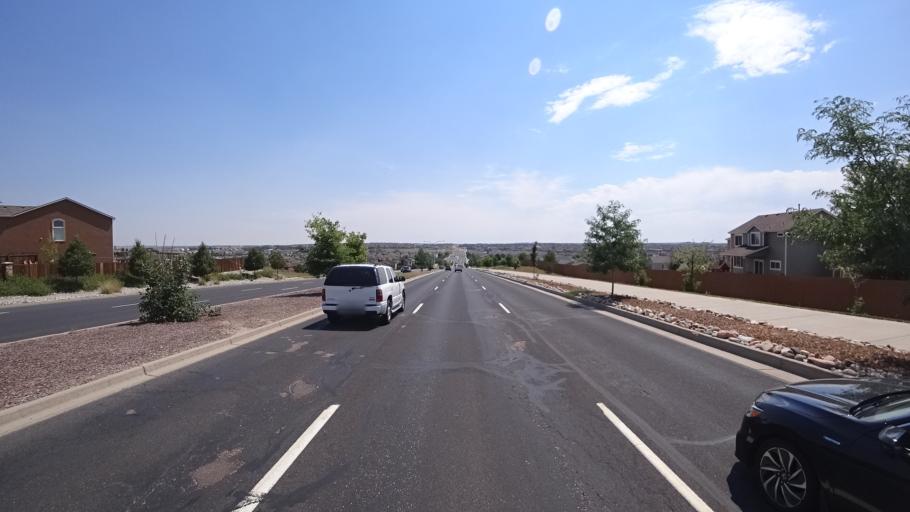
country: US
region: Colorado
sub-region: El Paso County
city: Cimarron Hills
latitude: 38.9259
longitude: -104.7063
